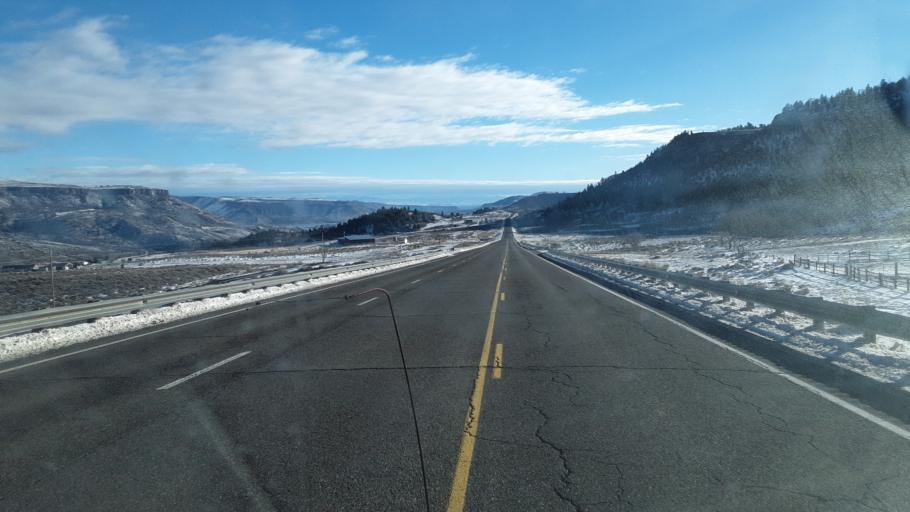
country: US
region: Colorado
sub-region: Hinsdale County
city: Lake City
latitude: 38.4378
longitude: -107.3926
